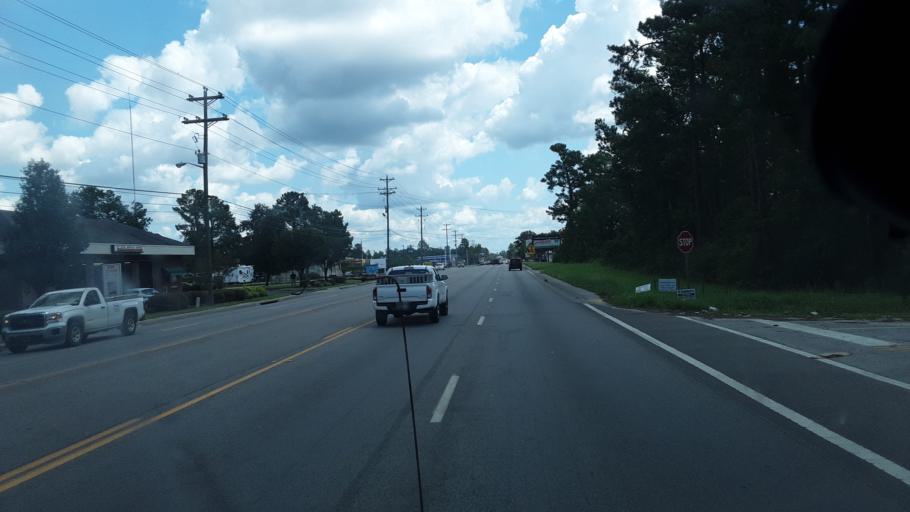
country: US
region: South Carolina
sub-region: Berkeley County
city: Sangaree
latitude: 33.0432
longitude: -80.1244
